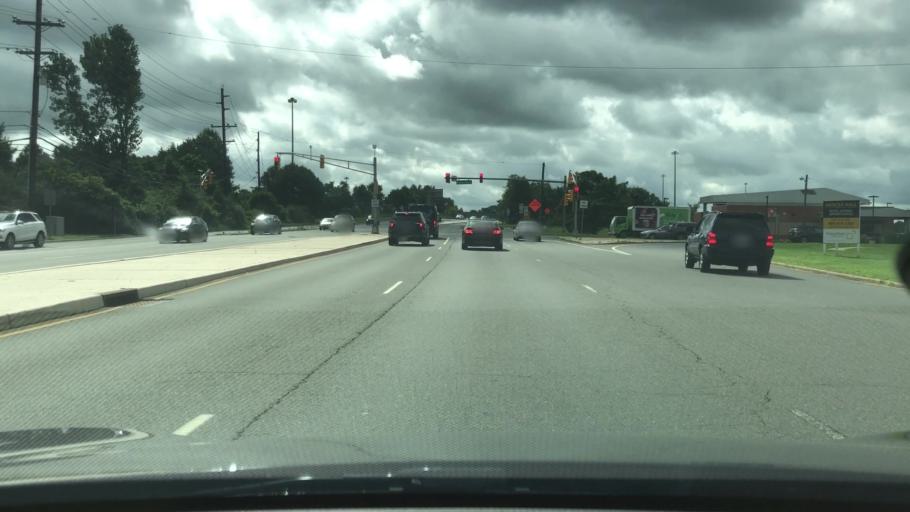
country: US
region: New Jersey
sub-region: Mercer County
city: Lawrenceville
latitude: 40.3001
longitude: -74.6816
